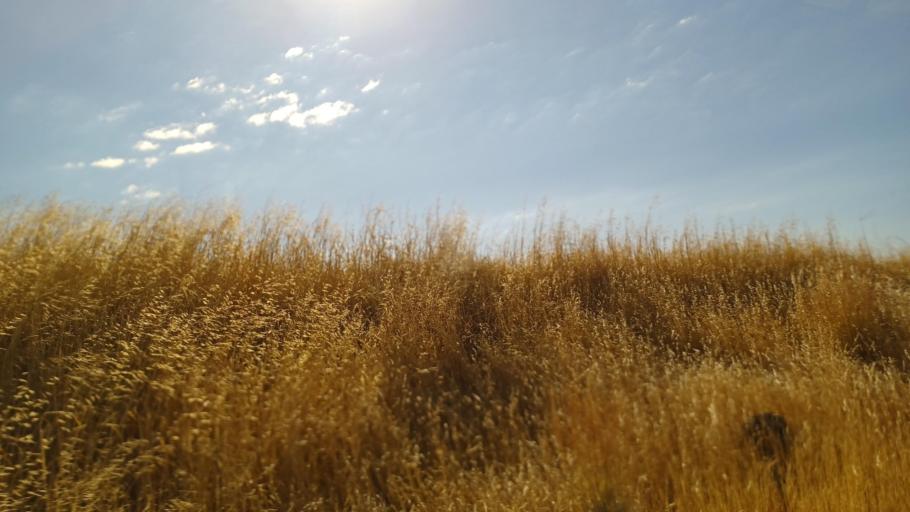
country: CY
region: Larnaka
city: Troulloi
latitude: 35.0038
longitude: 33.5919
